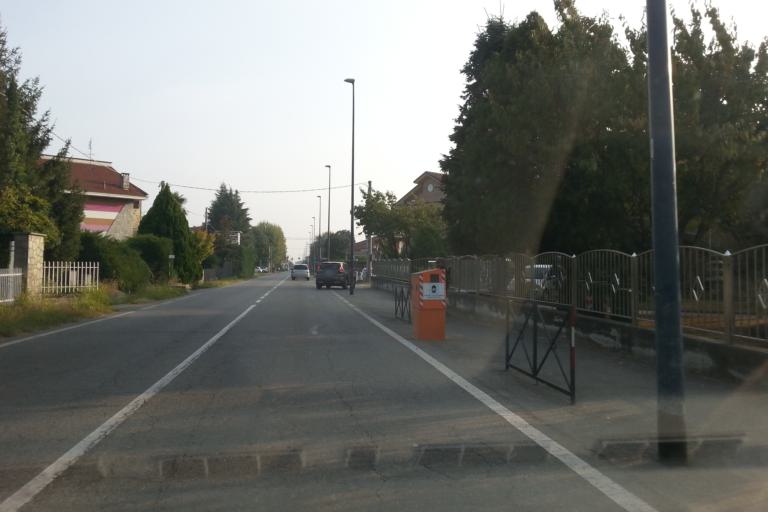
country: IT
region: Piedmont
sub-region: Provincia di Torino
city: Piossasco
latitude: 44.9955
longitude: 7.4676
